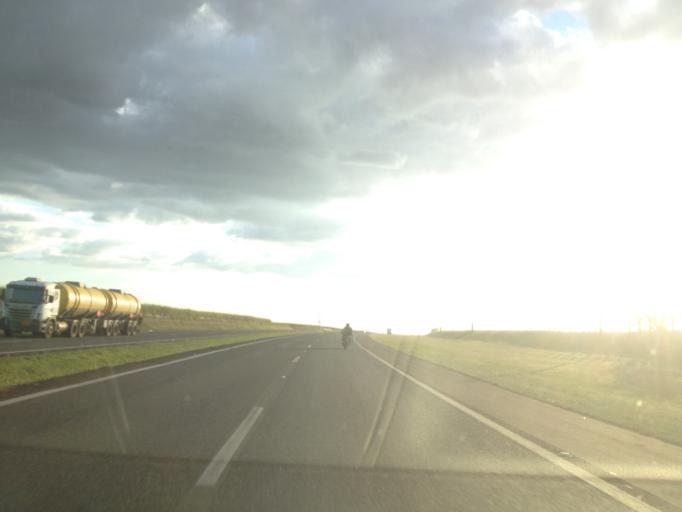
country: BR
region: Sao Paulo
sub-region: Jau
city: Jau
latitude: -22.2709
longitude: -48.4687
